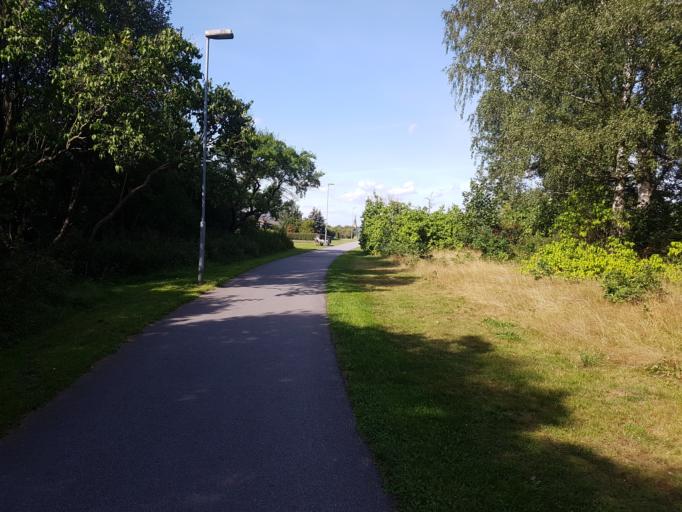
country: SE
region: Skane
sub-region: Sjobo Kommun
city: Sjoebo
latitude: 55.6365
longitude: 13.6989
